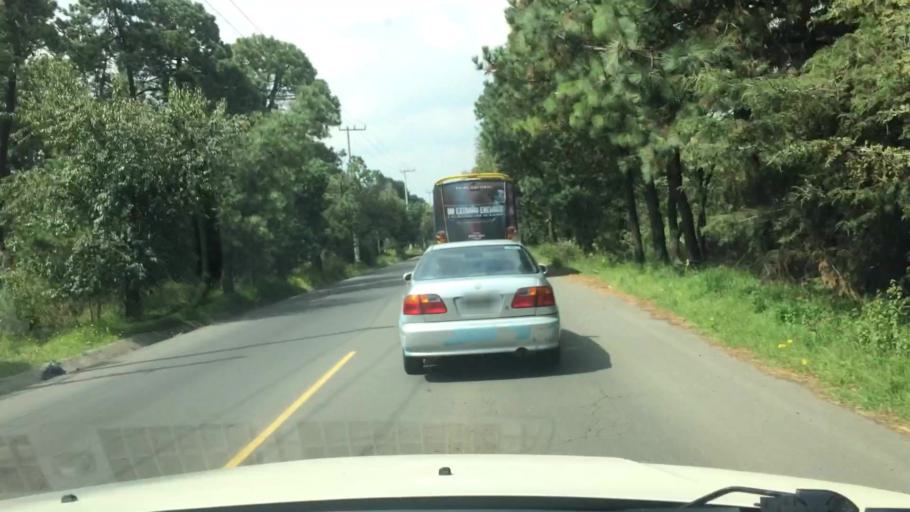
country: MX
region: Mexico City
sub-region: Tlalpan
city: Lomas de Tepemecatl
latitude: 19.2476
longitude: -99.2424
